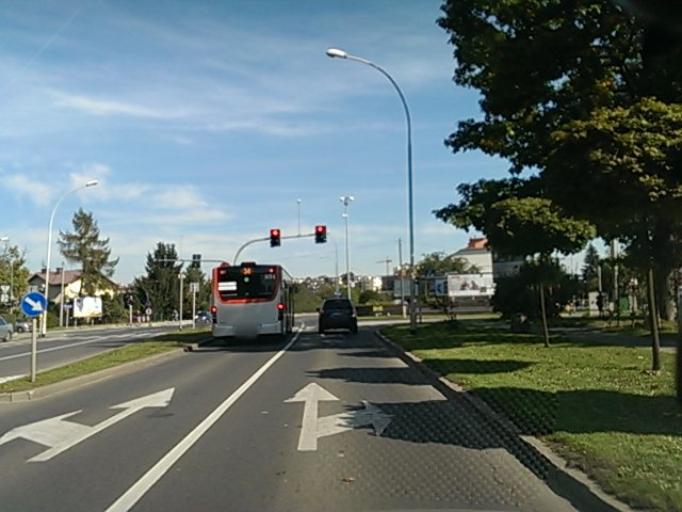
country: PL
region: Subcarpathian Voivodeship
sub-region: Rzeszow
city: Rzeszow
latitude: 50.0310
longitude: 22.0254
